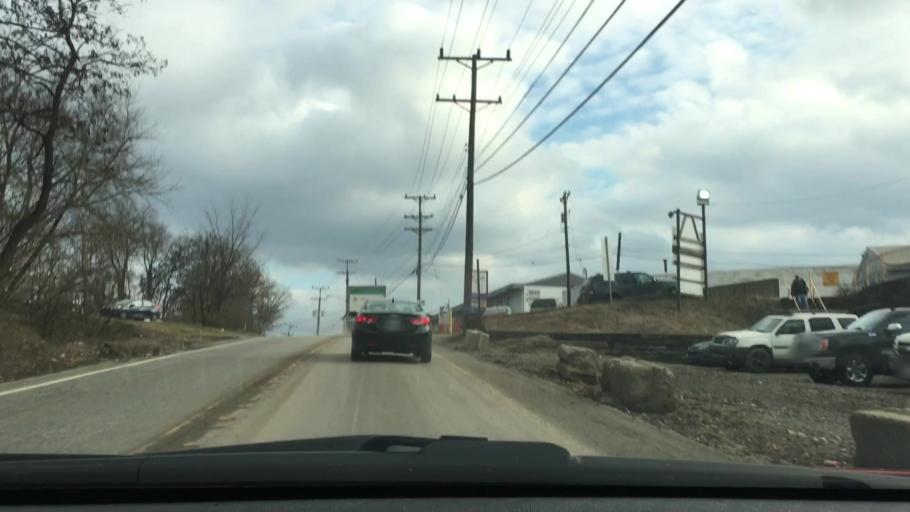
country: US
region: Pennsylvania
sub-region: Allegheny County
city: Pleasant Hills
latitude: 40.3513
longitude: -79.9516
